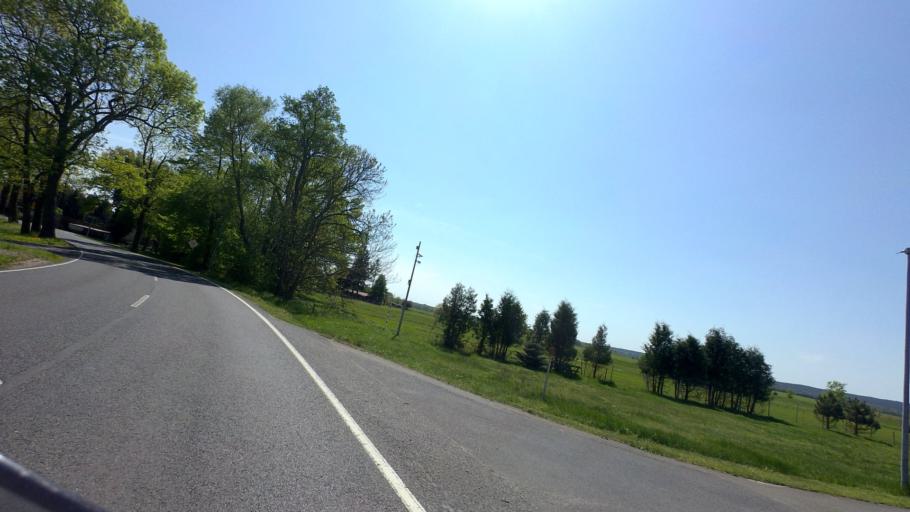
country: DE
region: Brandenburg
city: Schlepzig
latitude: 52.0822
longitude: 13.8719
